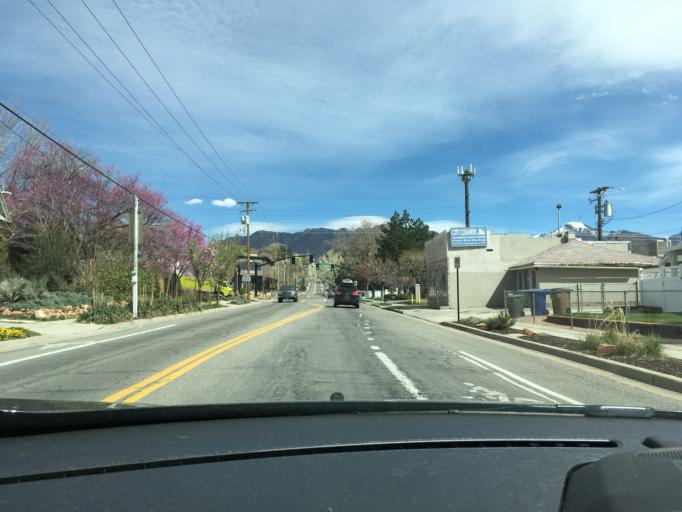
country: US
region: Utah
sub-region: Salt Lake County
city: South Salt Lake
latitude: 40.7416
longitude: -111.8609
